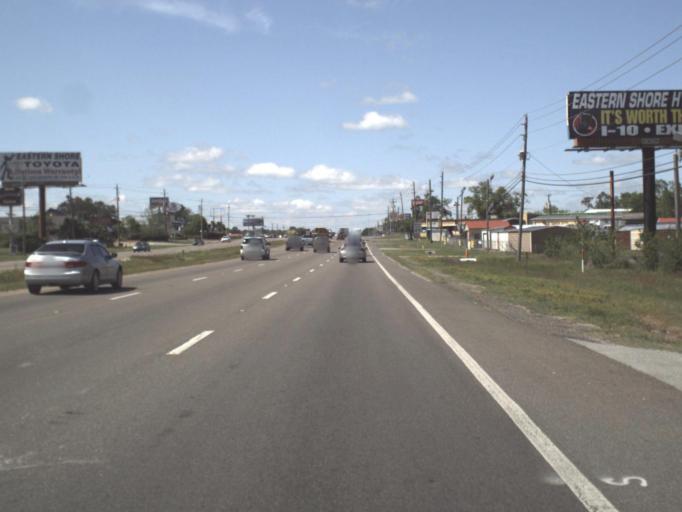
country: US
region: Florida
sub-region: Escambia County
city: Brent
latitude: 30.4869
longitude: -87.2586
